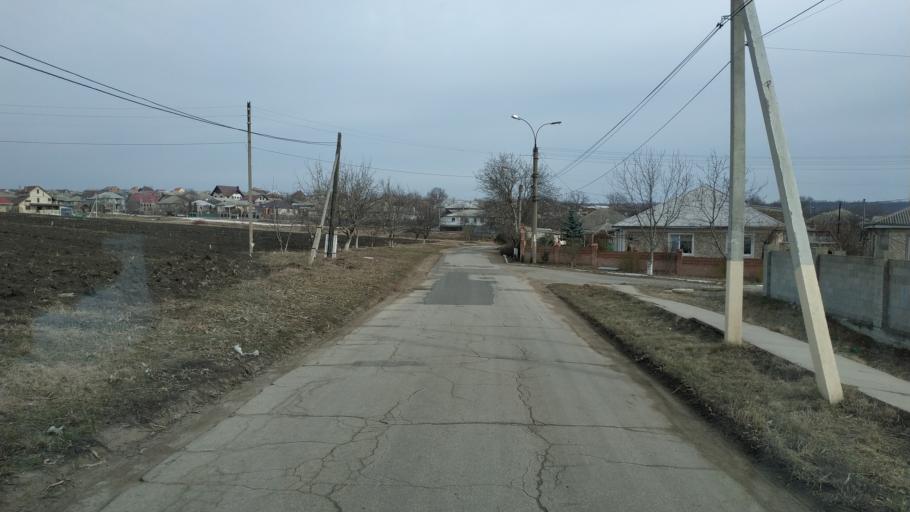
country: MD
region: Chisinau
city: Vatra
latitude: 47.0939
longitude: 28.7612
